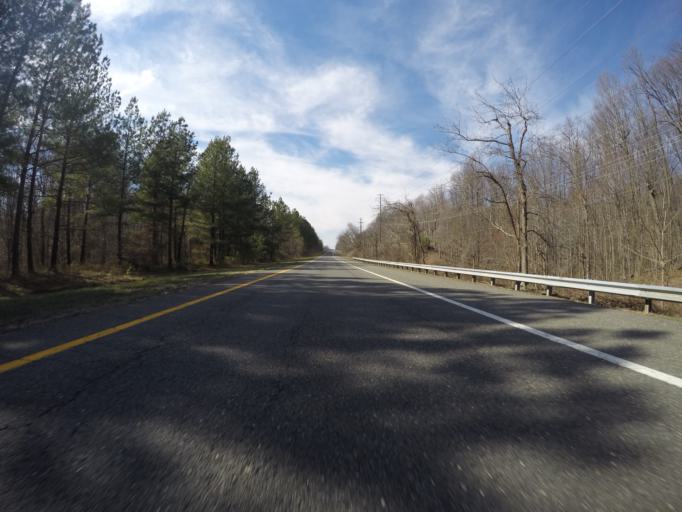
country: US
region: Maryland
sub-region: Anne Arundel County
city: Crownsville
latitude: 39.0433
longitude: -76.6116
